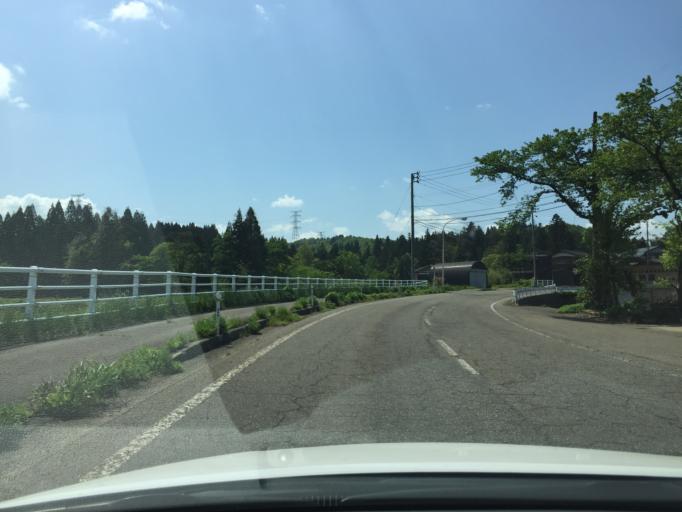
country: JP
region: Niigata
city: Tochio-honcho
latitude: 37.5429
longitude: 139.0934
